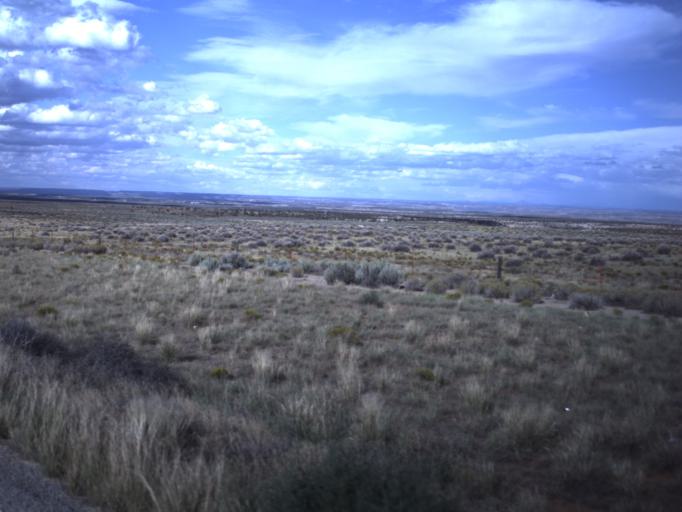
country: US
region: Utah
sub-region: San Juan County
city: Blanding
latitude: 37.3416
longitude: -109.3490
